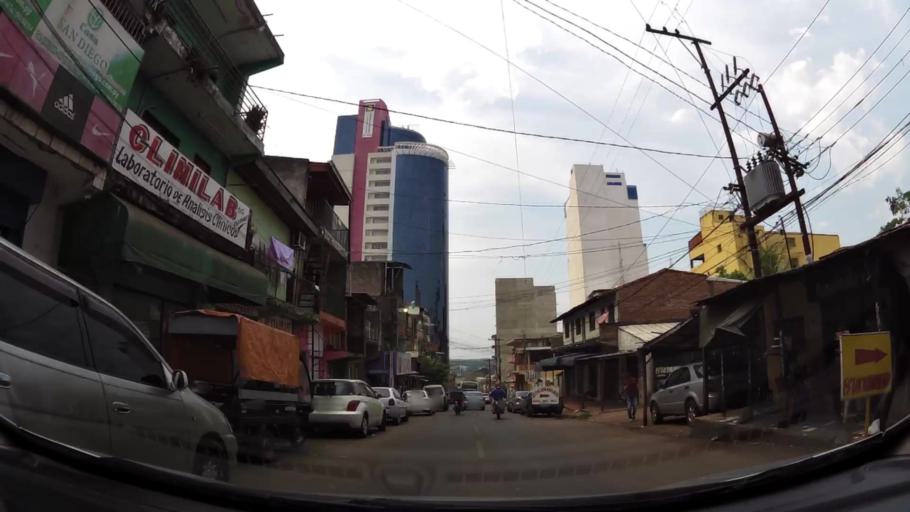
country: PY
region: Alto Parana
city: Ciudad del Este
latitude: -25.5077
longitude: -54.6118
